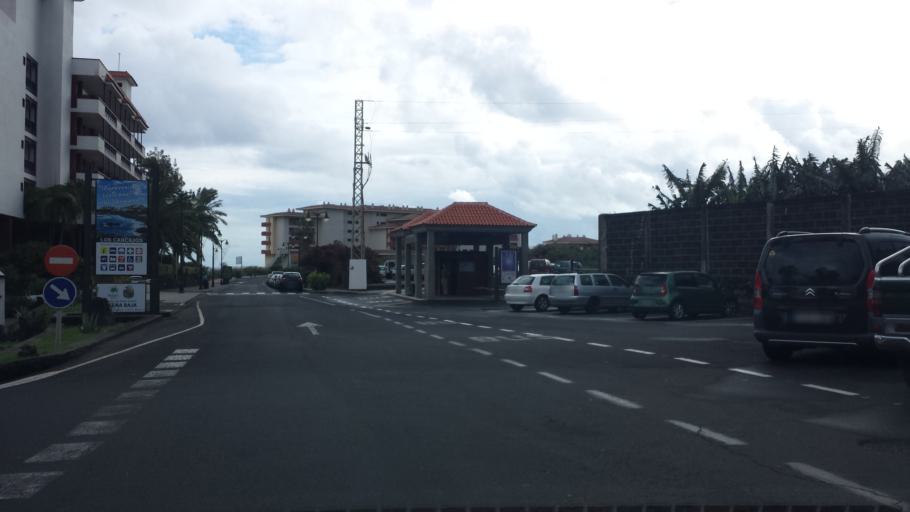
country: ES
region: Canary Islands
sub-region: Provincia de Santa Cruz de Tenerife
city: Brena Alta
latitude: 28.6508
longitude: -17.7608
